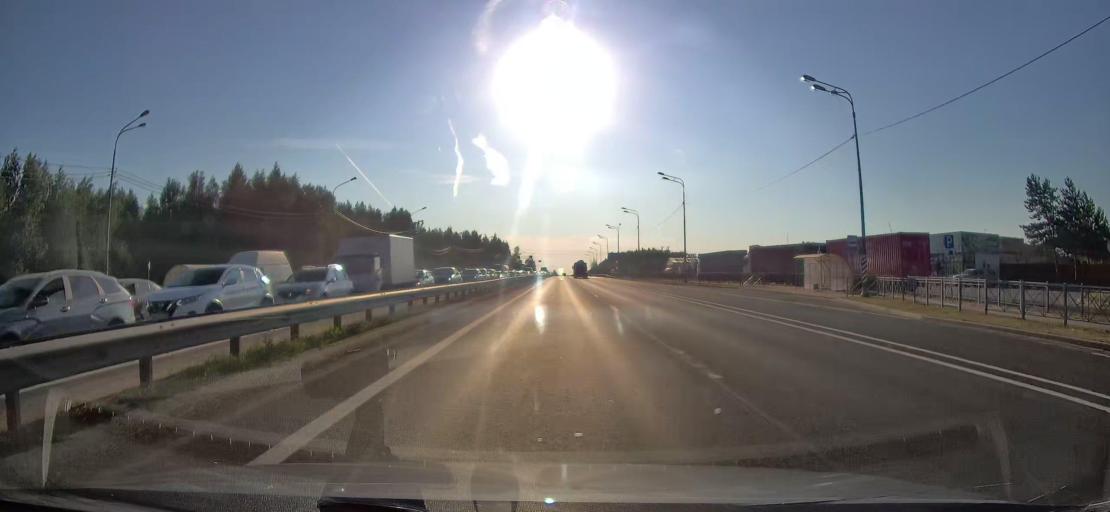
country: RU
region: Leningrad
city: Koltushi
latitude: 59.8979
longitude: 30.6860
